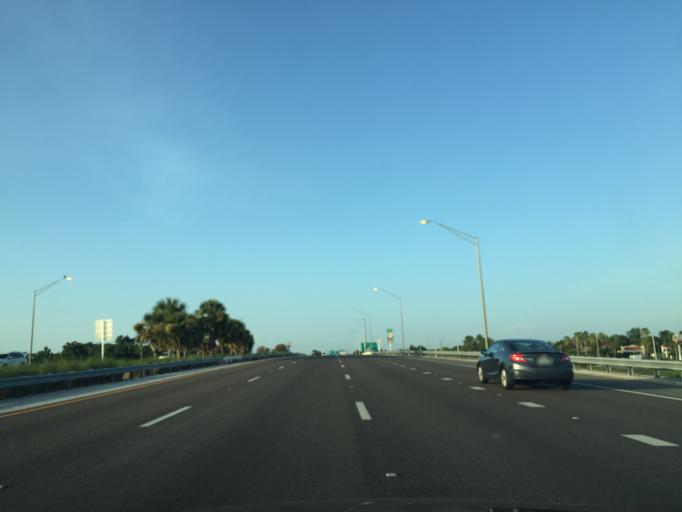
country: US
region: Florida
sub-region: Orange County
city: Union Park
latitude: 28.5703
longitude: -81.2659
